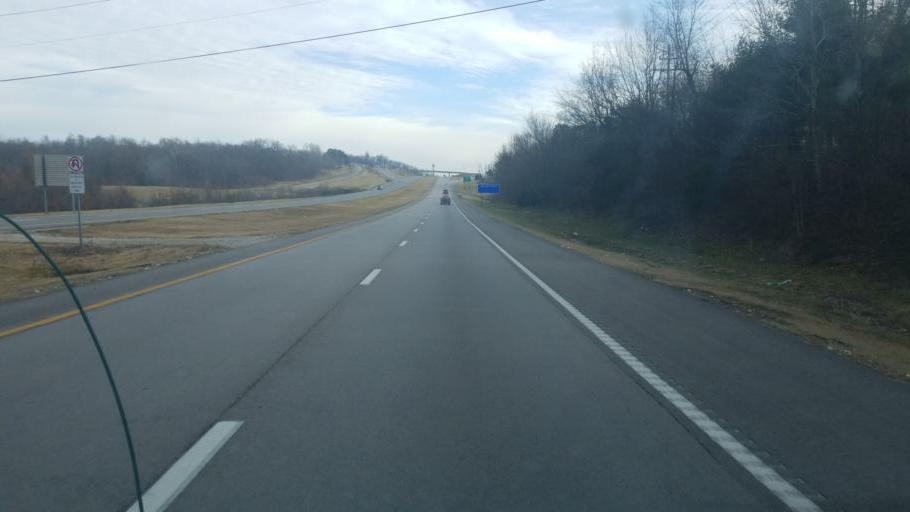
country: US
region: Missouri
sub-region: Stoddard County
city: Dexter
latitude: 36.8138
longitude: -89.9517
